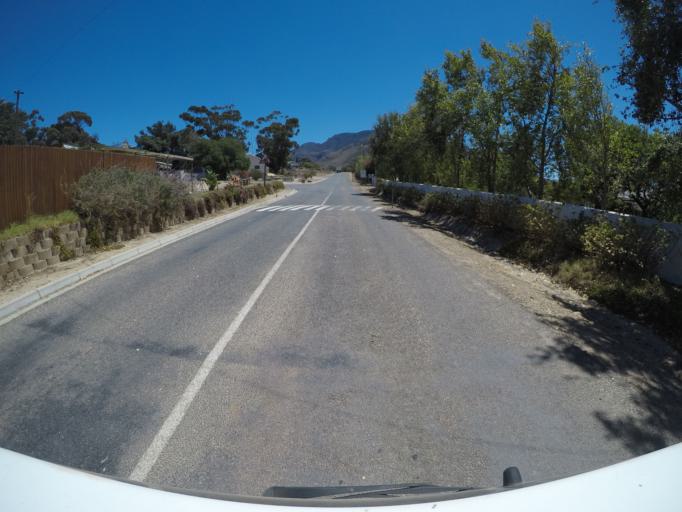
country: ZA
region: Western Cape
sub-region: Overberg District Municipality
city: Hermanus
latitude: -34.2262
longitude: 19.2074
